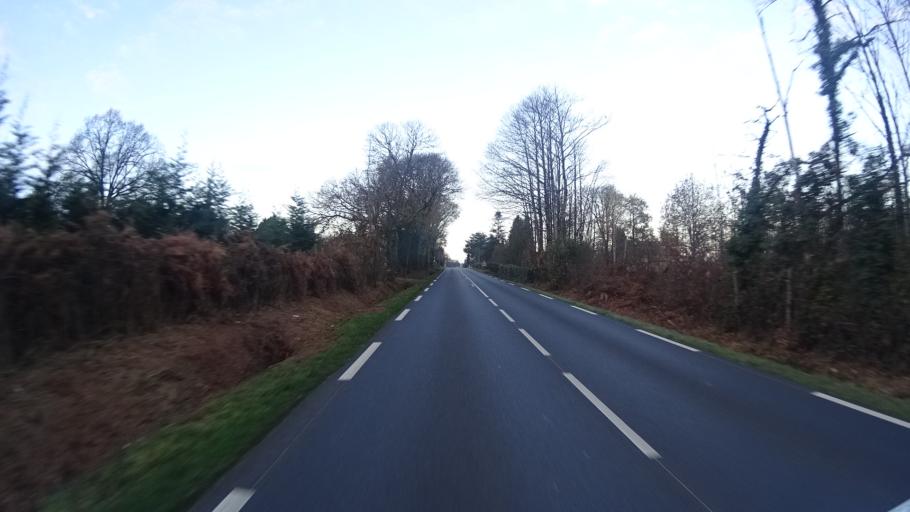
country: FR
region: Pays de la Loire
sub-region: Departement de la Loire-Atlantique
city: Saint-Nicolas-de-Redon
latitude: 47.6426
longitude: -2.0416
